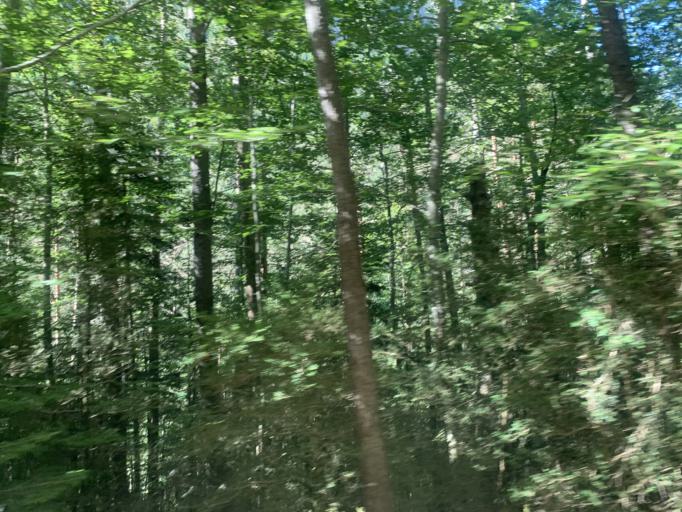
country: ES
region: Aragon
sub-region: Provincia de Huesca
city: Broto
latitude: 42.6523
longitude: -0.0747
